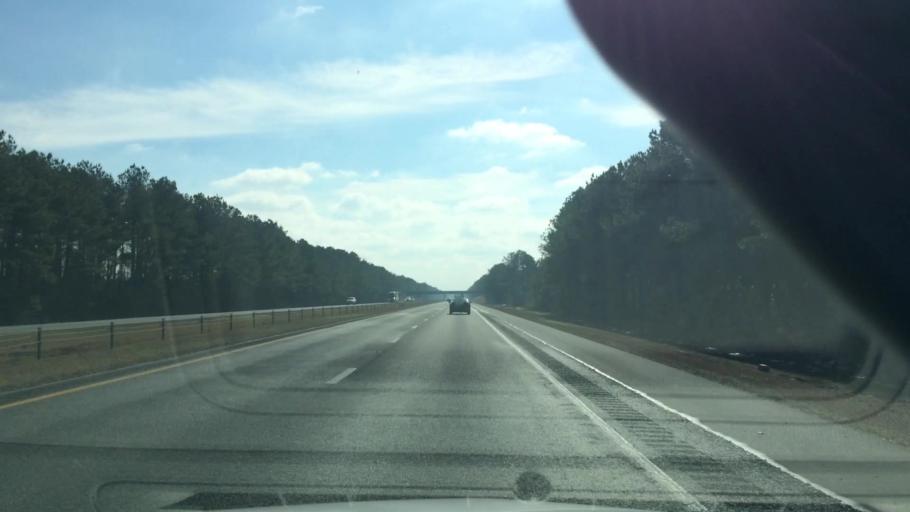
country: US
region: North Carolina
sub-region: Duplin County
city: Wallace
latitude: 34.7382
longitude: -77.9447
